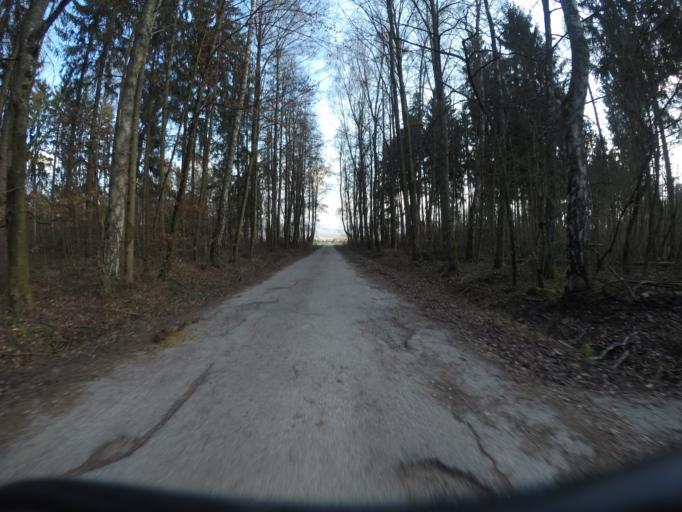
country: DE
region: Baden-Wuerttemberg
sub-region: Tuebingen Region
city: Dusslingen
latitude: 48.4563
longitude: 9.0256
